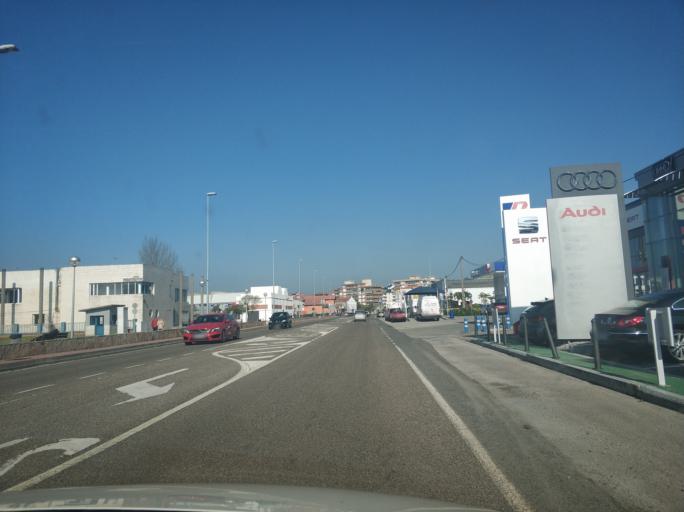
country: ES
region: Cantabria
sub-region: Provincia de Cantabria
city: Colindres
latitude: 43.3941
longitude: -3.4605
